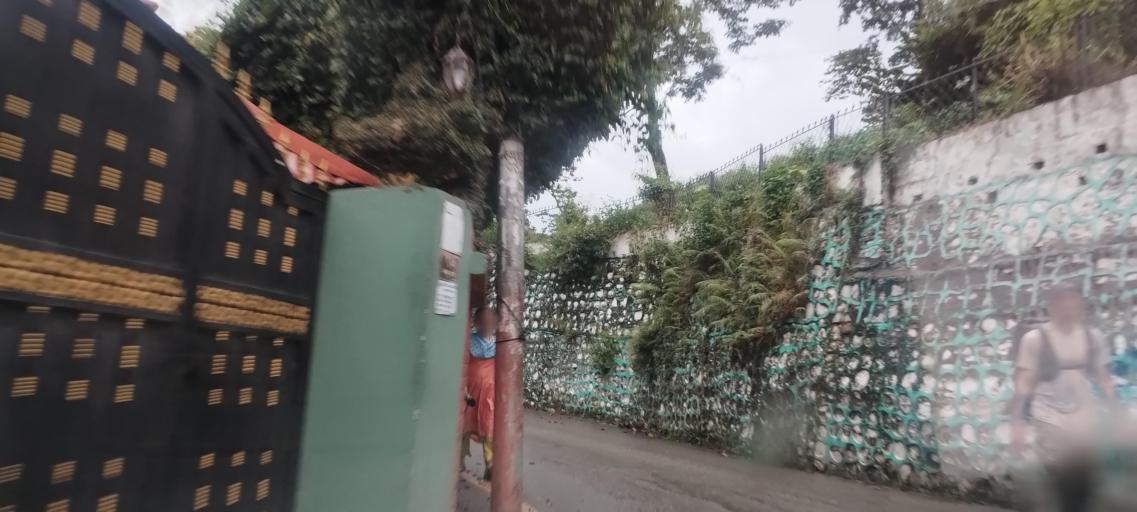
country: NP
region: Central Region
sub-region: Bagmati Zone
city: Kathmandu
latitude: 27.7088
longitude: 85.3402
